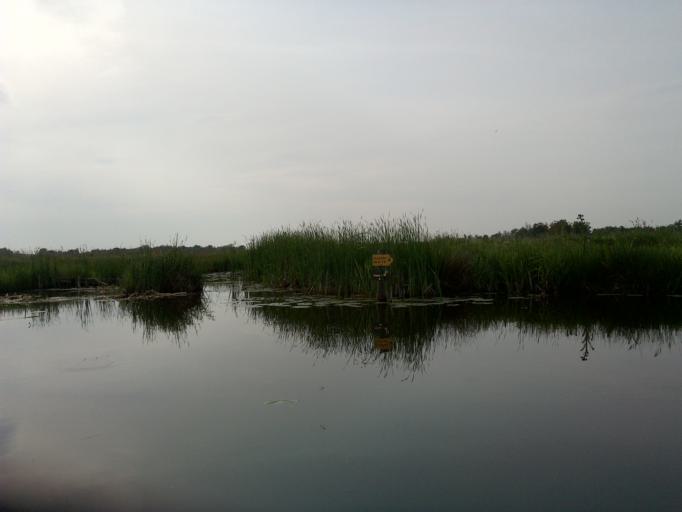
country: NL
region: South Holland
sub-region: Gemeente Nieuwkoop
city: Nieuwkoop
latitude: 52.1389
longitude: 4.7958
